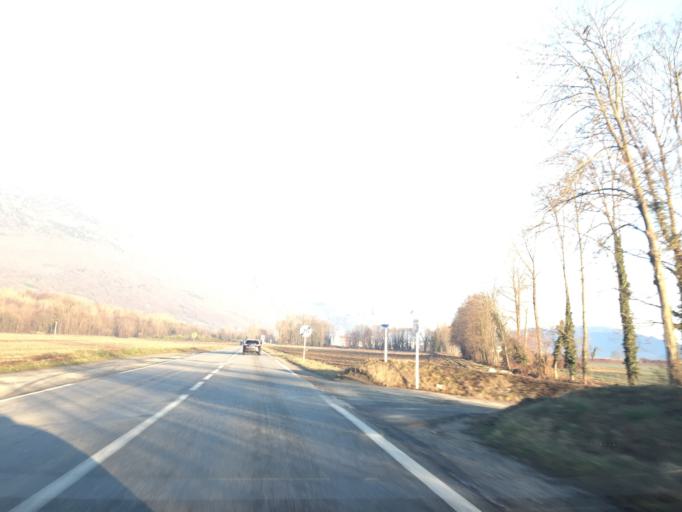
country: FR
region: Rhone-Alpes
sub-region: Departement de la Savoie
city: Le Bourget-du-Lac
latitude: 45.6300
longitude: 5.8751
